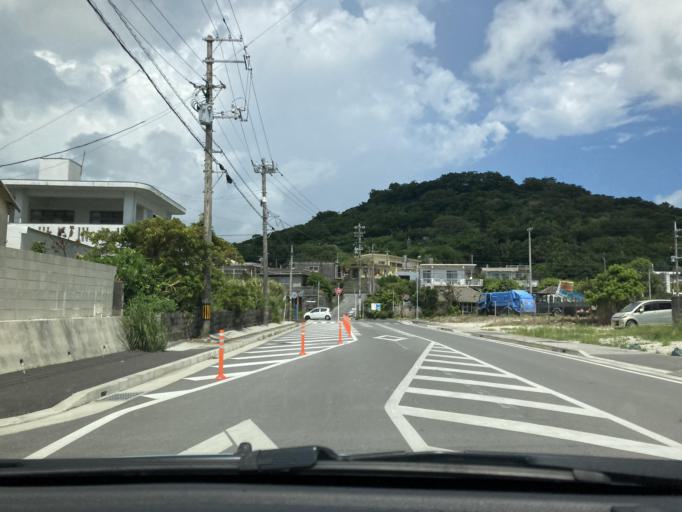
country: JP
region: Okinawa
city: Tomigusuku
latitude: 26.1629
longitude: 127.7567
